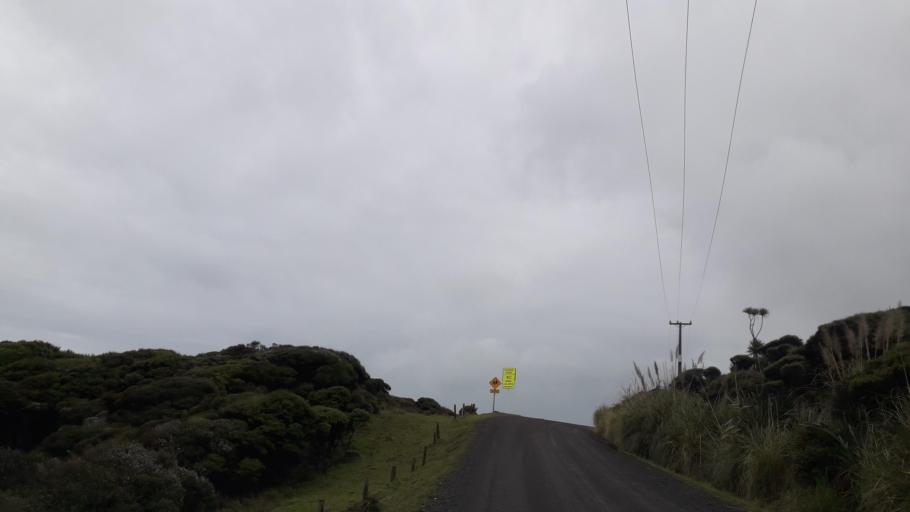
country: NZ
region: Northland
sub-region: Far North District
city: Ahipara
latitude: -35.4381
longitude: 173.2869
